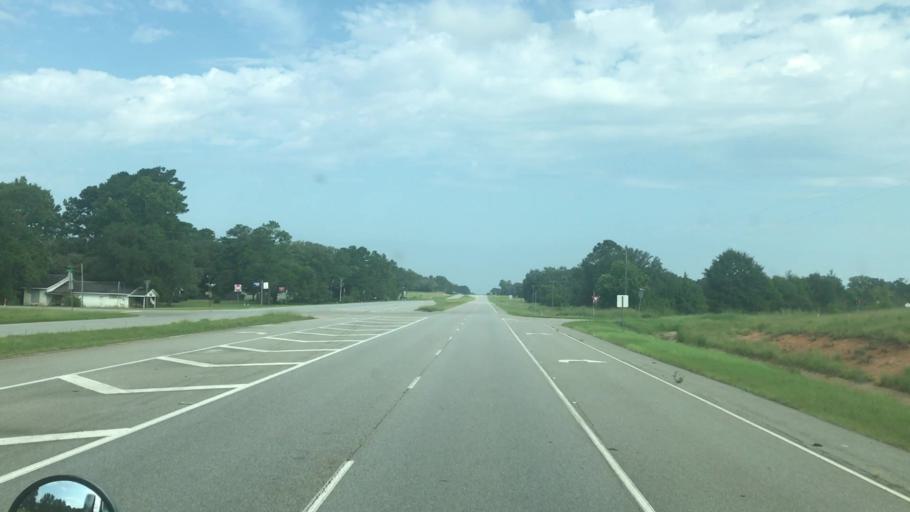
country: US
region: Georgia
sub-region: Early County
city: Blakely
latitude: 31.3032
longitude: -84.8628
